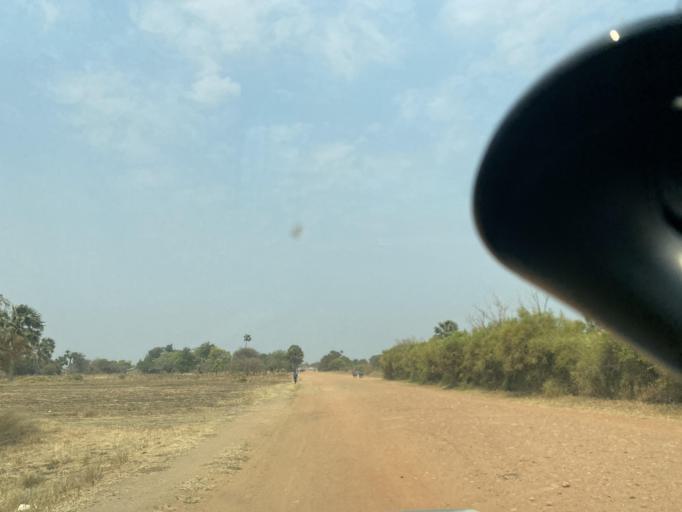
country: ZM
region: Lusaka
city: Kafue
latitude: -15.6585
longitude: 28.0266
